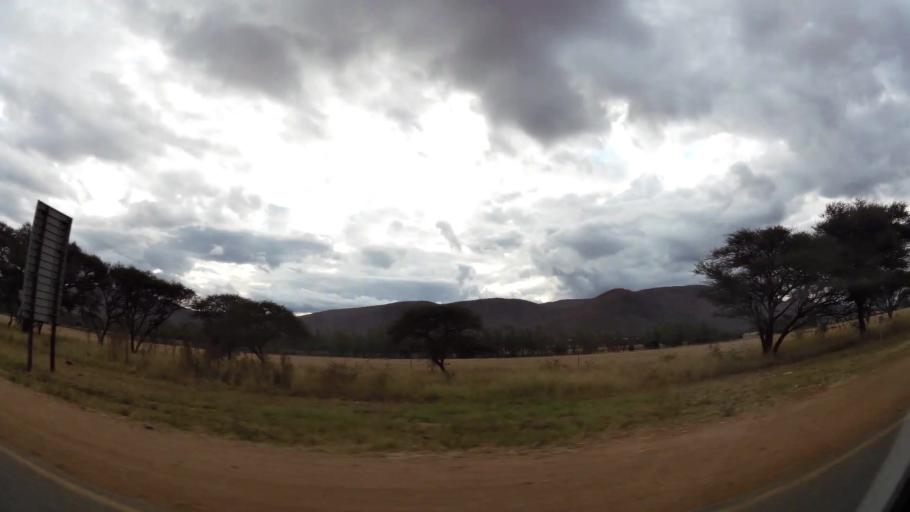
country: ZA
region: Limpopo
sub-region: Waterberg District Municipality
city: Mokopane
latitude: -24.2687
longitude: 28.9821
